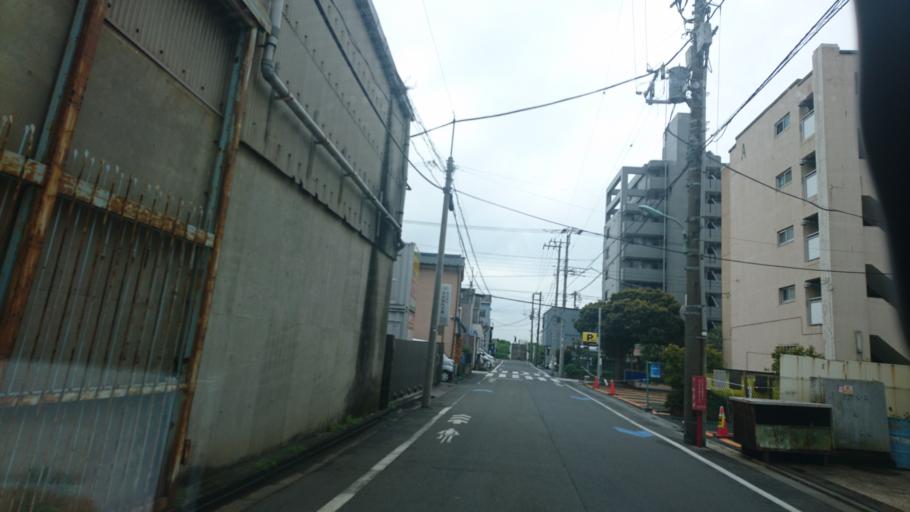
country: JP
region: Kanagawa
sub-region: Kawasaki-shi
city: Kawasaki
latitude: 35.5464
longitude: 139.7279
